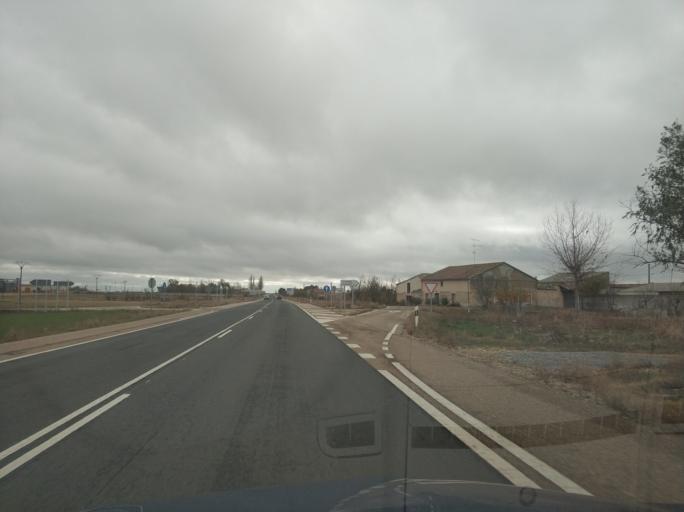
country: ES
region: Castille and Leon
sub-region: Provincia de Salamanca
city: Pedrosillo el Ralo
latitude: 41.0635
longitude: -5.5441
